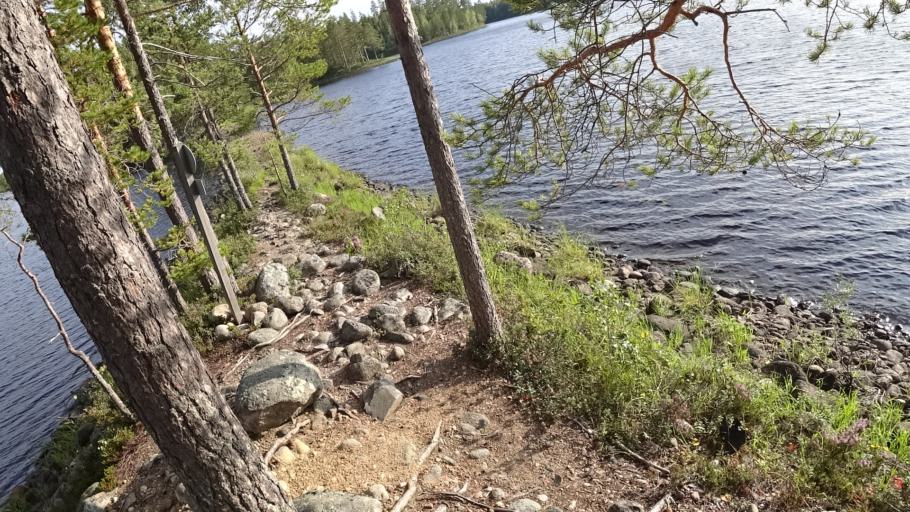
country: FI
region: North Karelia
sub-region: Joensuu
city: Ilomantsi
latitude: 62.5653
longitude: 31.1829
